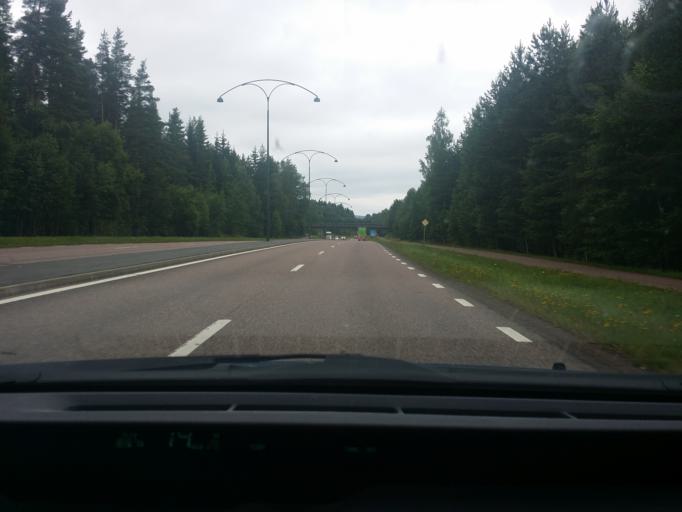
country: SE
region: Dalarna
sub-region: Borlange Kommun
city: Borlaenge
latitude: 60.5028
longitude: 15.3912
